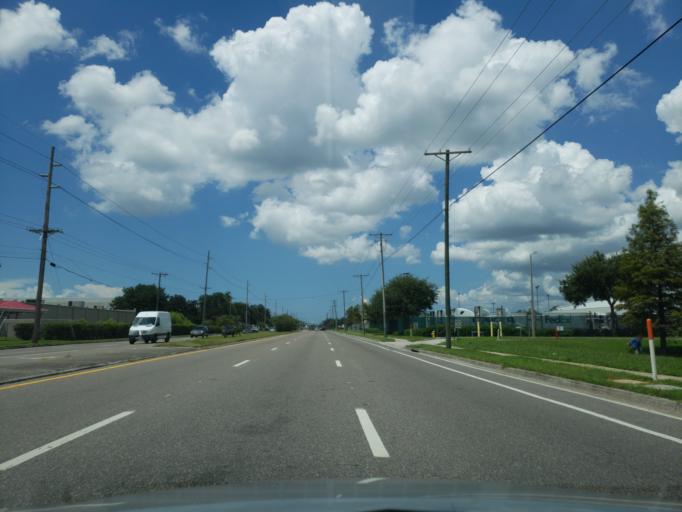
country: US
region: Florida
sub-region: Hillsborough County
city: Egypt Lake-Leto
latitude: 28.0256
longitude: -82.5304
